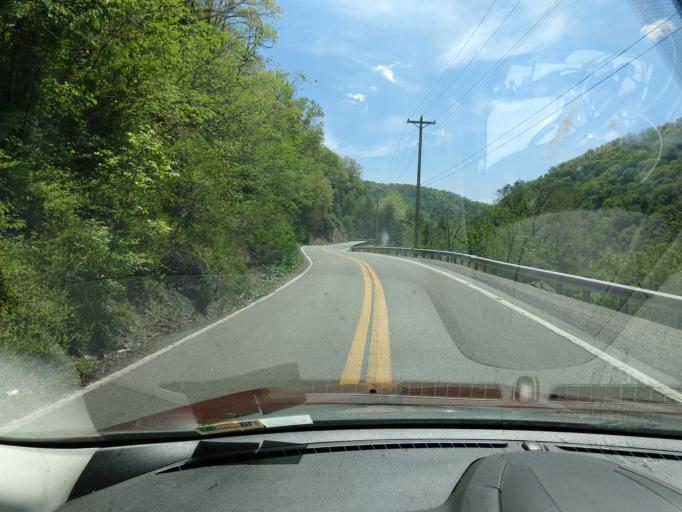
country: US
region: West Virginia
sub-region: McDowell County
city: Welch
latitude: 37.3102
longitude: -81.6934
